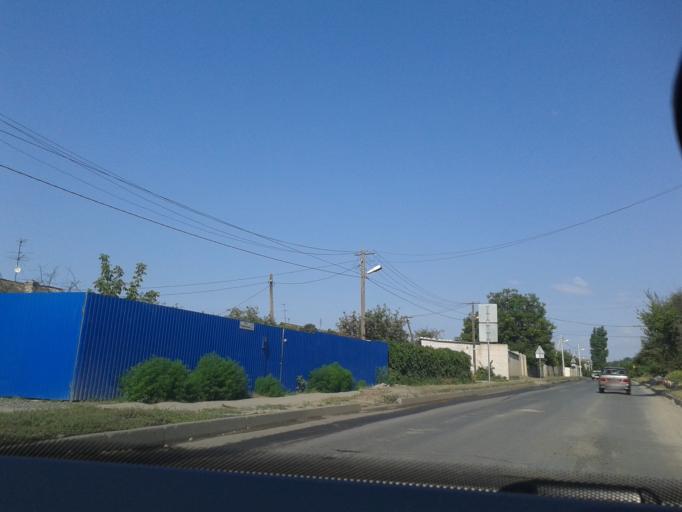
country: RU
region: Volgograd
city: Volgograd
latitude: 48.6939
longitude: 44.4513
